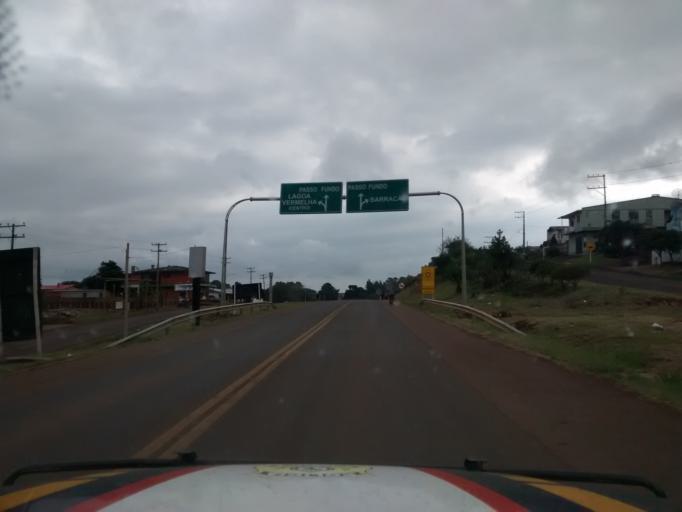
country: BR
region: Rio Grande do Sul
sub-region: Lagoa Vermelha
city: Lagoa Vermelha
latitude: -28.2042
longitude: -51.5231
